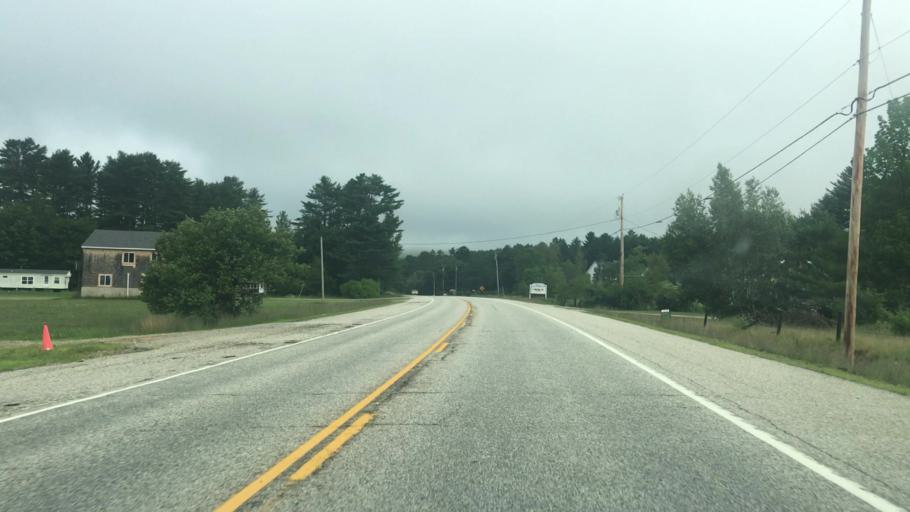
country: US
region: Maine
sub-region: Oxford County
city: Paris
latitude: 44.2770
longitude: -70.5146
